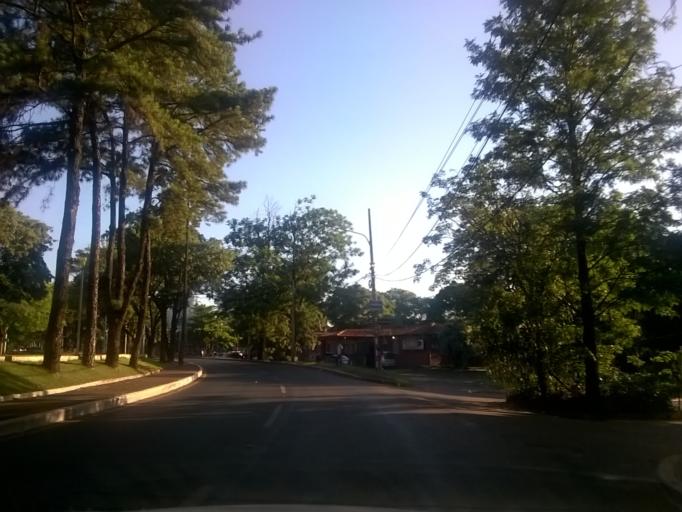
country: PY
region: Alto Parana
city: Ciudad del Este
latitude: -25.5152
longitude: -54.6158
